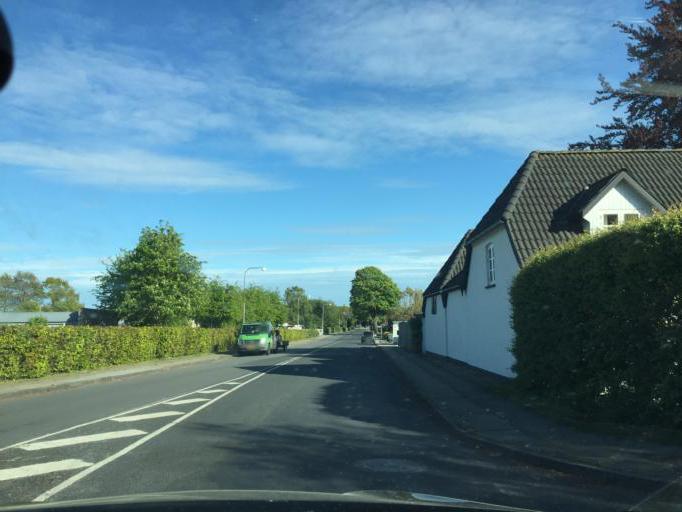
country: DK
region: South Denmark
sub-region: Odense Kommune
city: Bellinge
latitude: 55.3554
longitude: 10.3459
